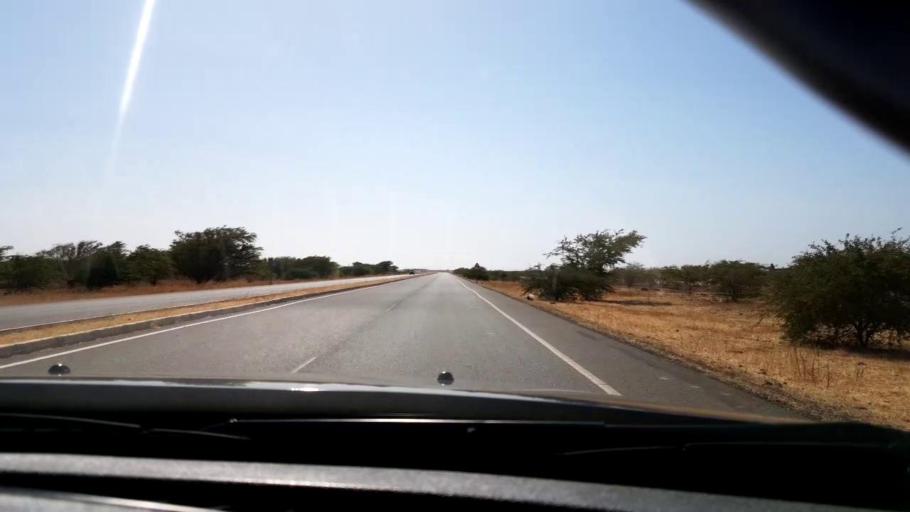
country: CV
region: Praia
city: Praia
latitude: 14.9477
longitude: -23.4907
